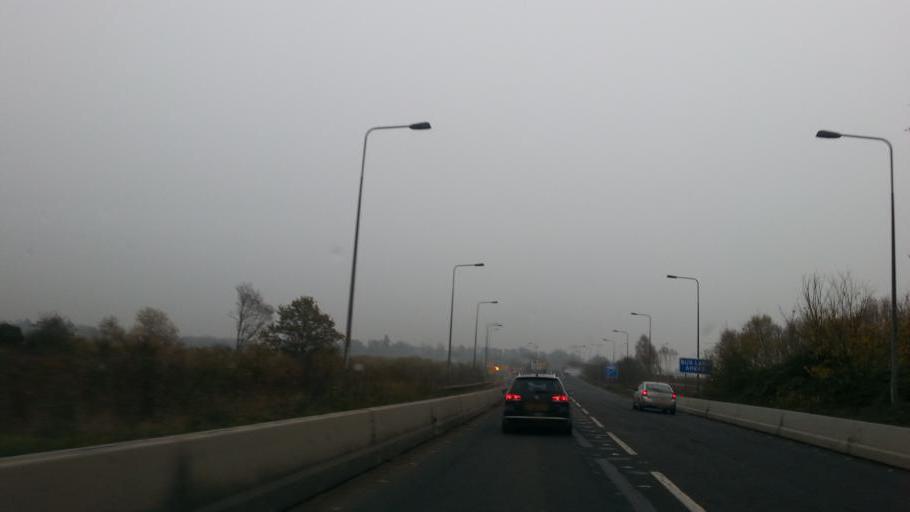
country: GB
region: England
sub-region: Cambridgeshire
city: Girton
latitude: 52.2343
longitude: 0.0704
